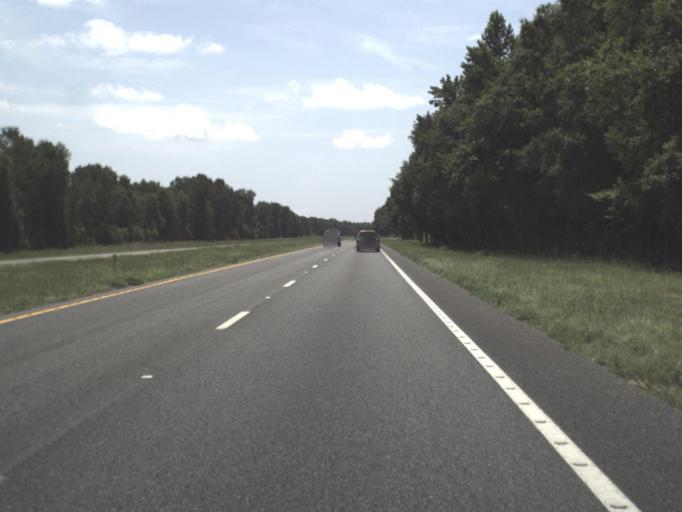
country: US
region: Florida
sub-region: Taylor County
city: Perry
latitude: 30.0003
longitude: -83.5080
